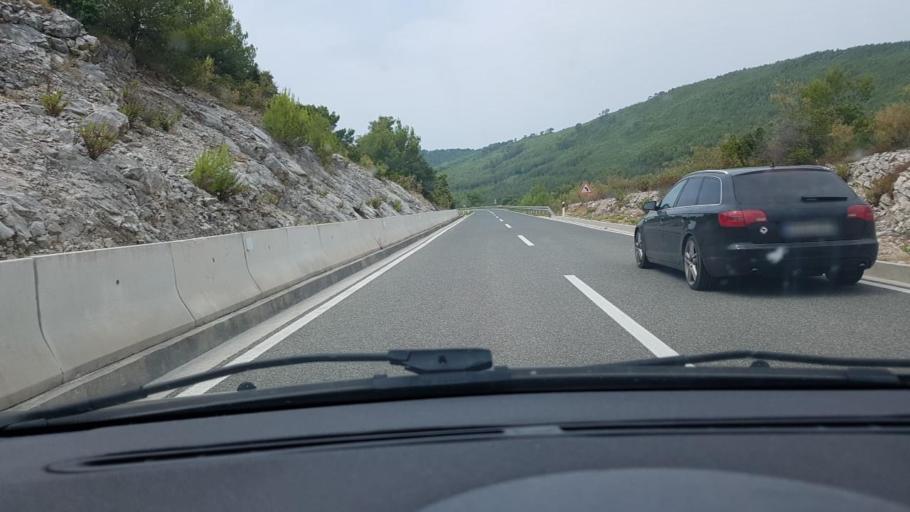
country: HR
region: Dubrovacko-Neretvanska
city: Smokvica
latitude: 42.9541
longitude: 16.9086
